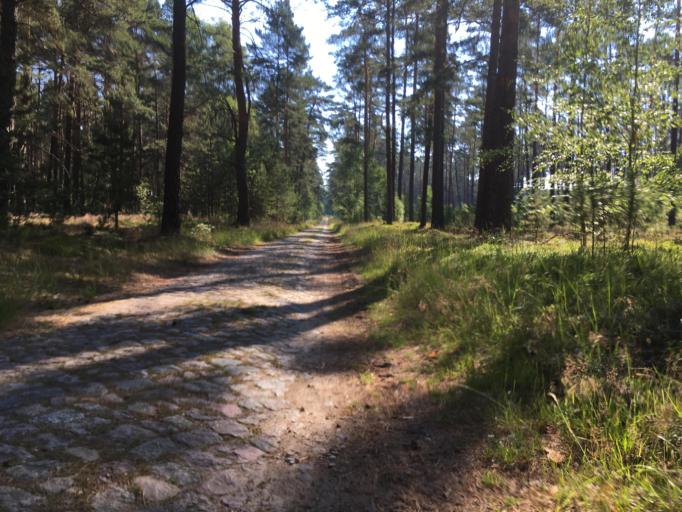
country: DE
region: Brandenburg
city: Joachimsthal
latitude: 52.9506
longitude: 13.6597
